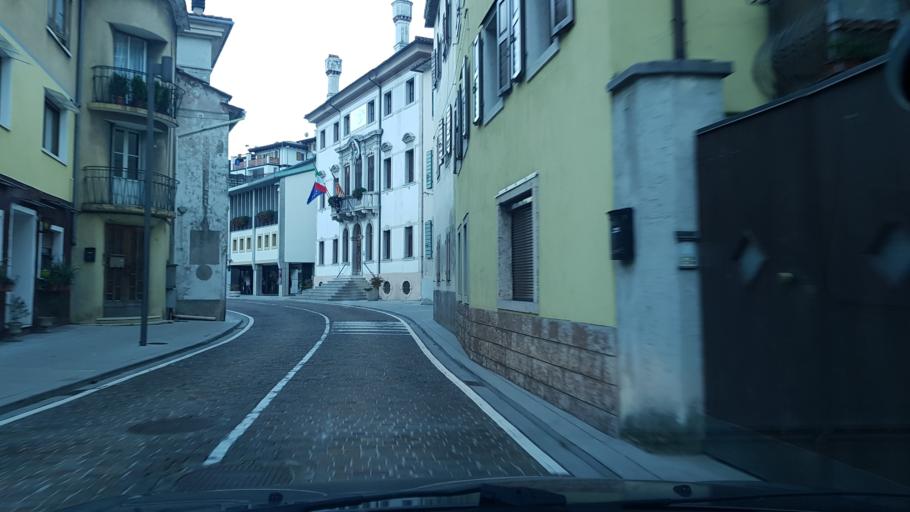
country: IT
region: Veneto
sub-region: Provincia di Belluno
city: Longarone
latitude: 46.2707
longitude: 12.3003
